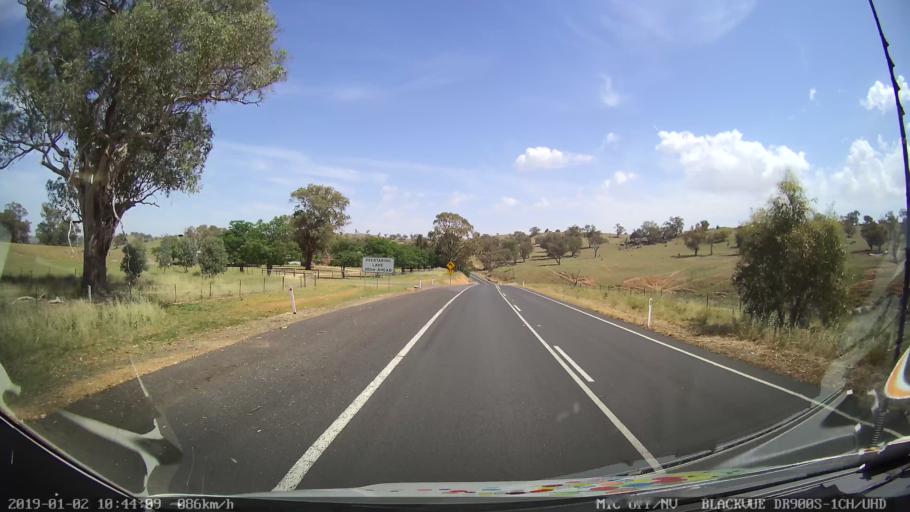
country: AU
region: New South Wales
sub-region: Cootamundra
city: Cootamundra
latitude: -34.7639
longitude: 148.2984
